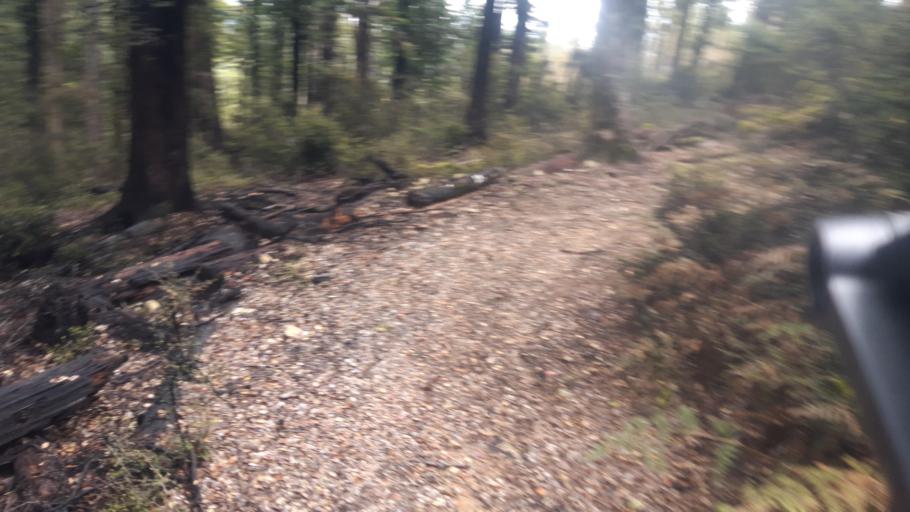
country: NZ
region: Tasman
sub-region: Tasman District
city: Wakefield
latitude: -41.7595
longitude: 172.8057
